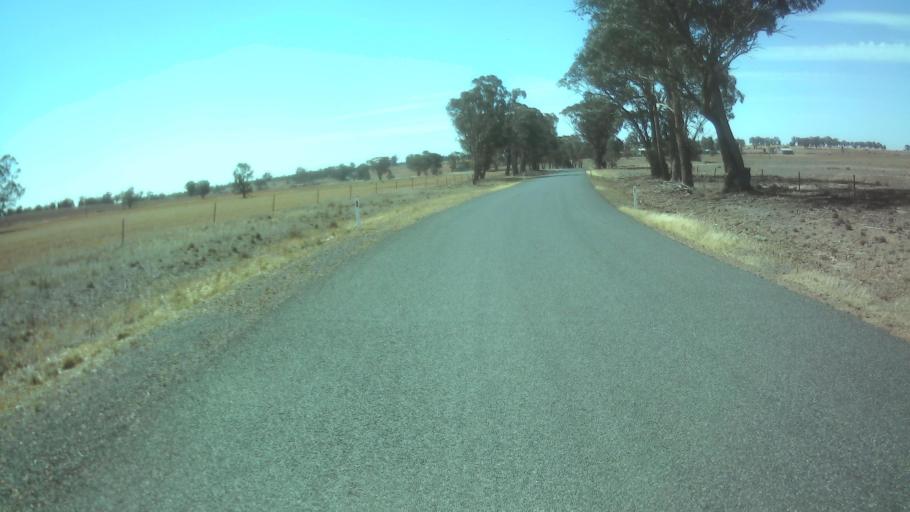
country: AU
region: New South Wales
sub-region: Weddin
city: Grenfell
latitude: -33.7664
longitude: 147.8651
